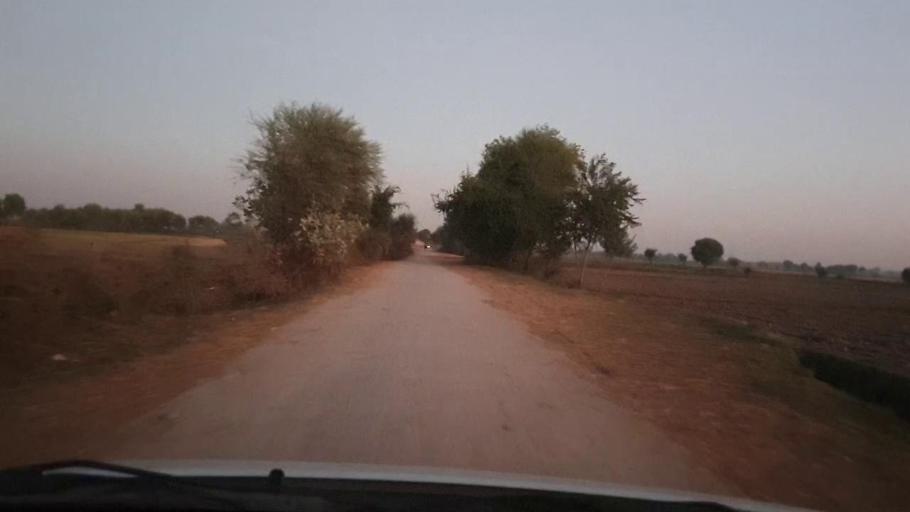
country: PK
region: Sindh
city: Khairpur Nathan Shah
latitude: 27.1332
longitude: 67.7237
